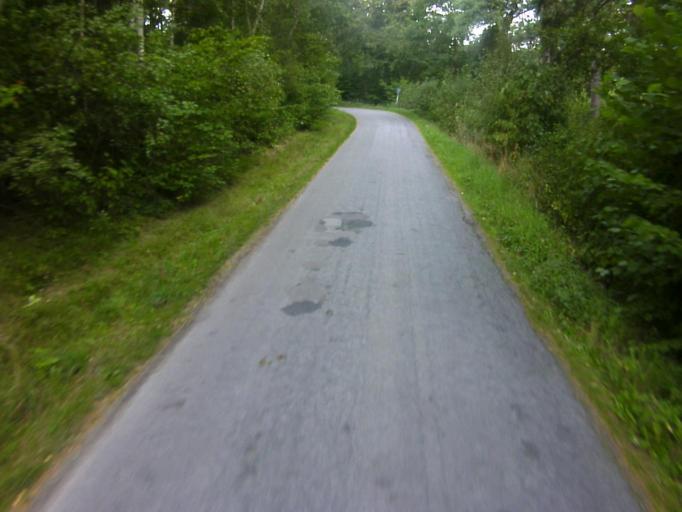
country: SE
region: Blekinge
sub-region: Solvesborgs Kommun
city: Soelvesborg
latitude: 56.0096
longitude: 14.6371
